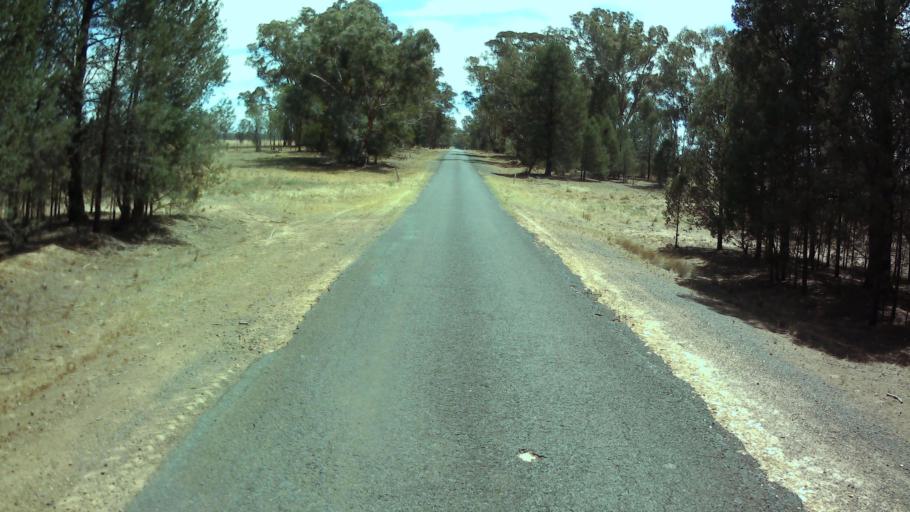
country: AU
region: New South Wales
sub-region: Weddin
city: Grenfell
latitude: -33.7572
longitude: 148.2059
